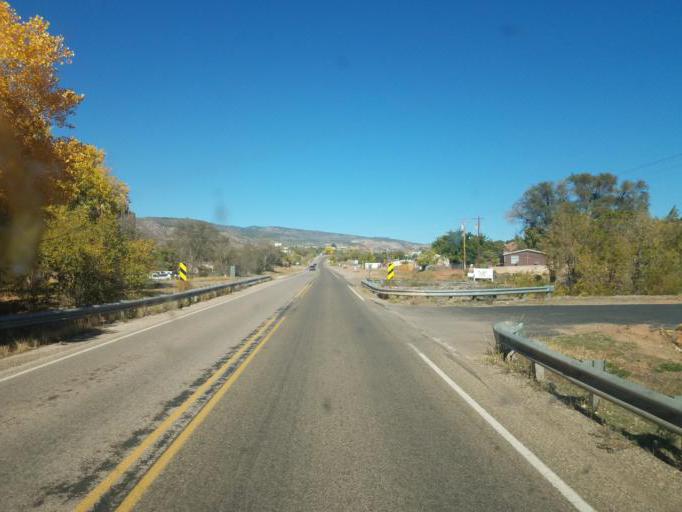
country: US
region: New Mexico
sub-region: Sandoval County
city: Jemez Pueblo
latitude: 35.6519
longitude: -106.7319
